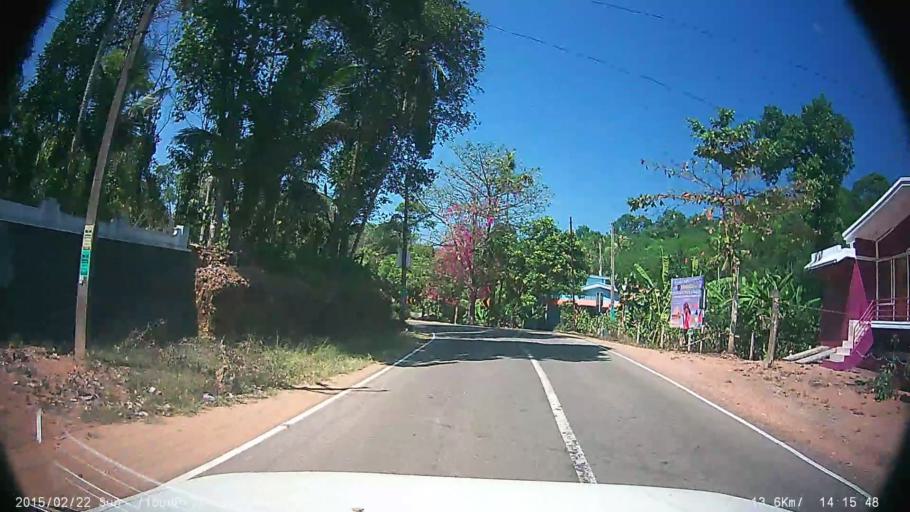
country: IN
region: Kerala
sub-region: Kottayam
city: Kottayam
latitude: 9.5530
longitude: 76.6819
